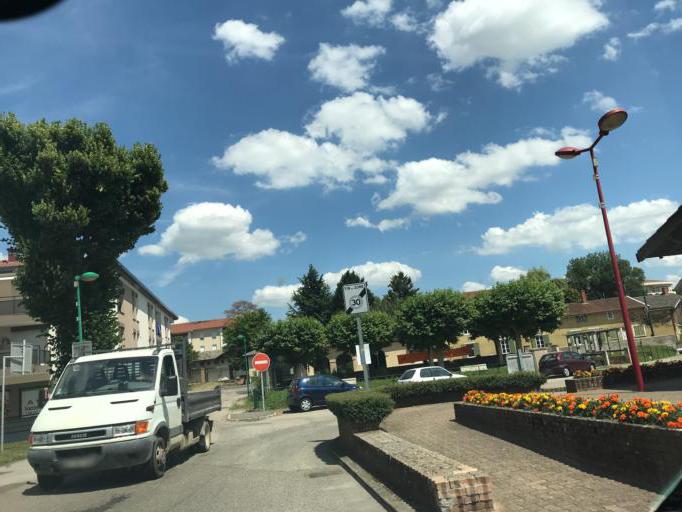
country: FR
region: Rhone-Alpes
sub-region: Departement de l'Ain
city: Mionnay
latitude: 45.8955
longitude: 4.9301
